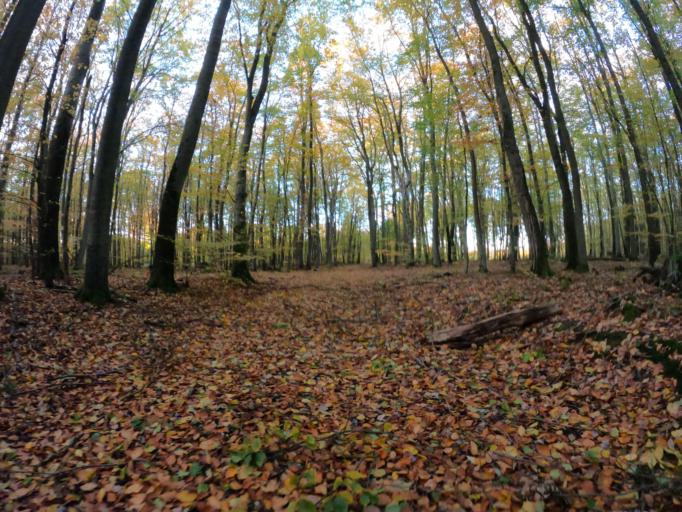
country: PL
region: West Pomeranian Voivodeship
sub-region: Powiat mysliborski
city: Barlinek
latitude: 52.9688
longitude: 15.2314
